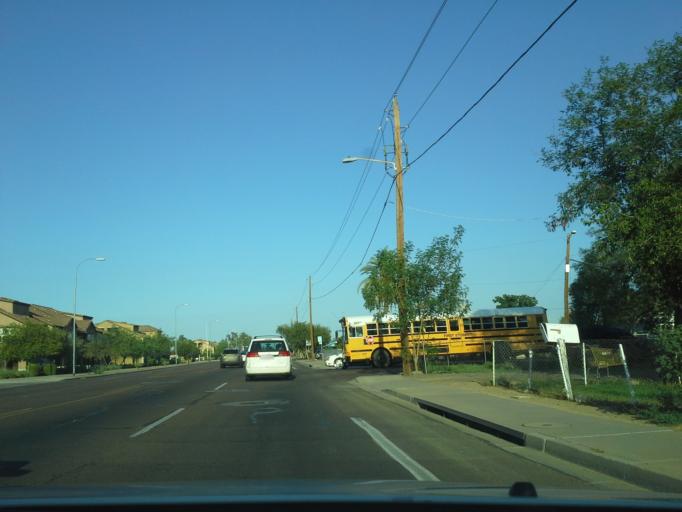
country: US
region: Arizona
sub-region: Maricopa County
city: Phoenix
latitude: 33.3930
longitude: -112.0348
